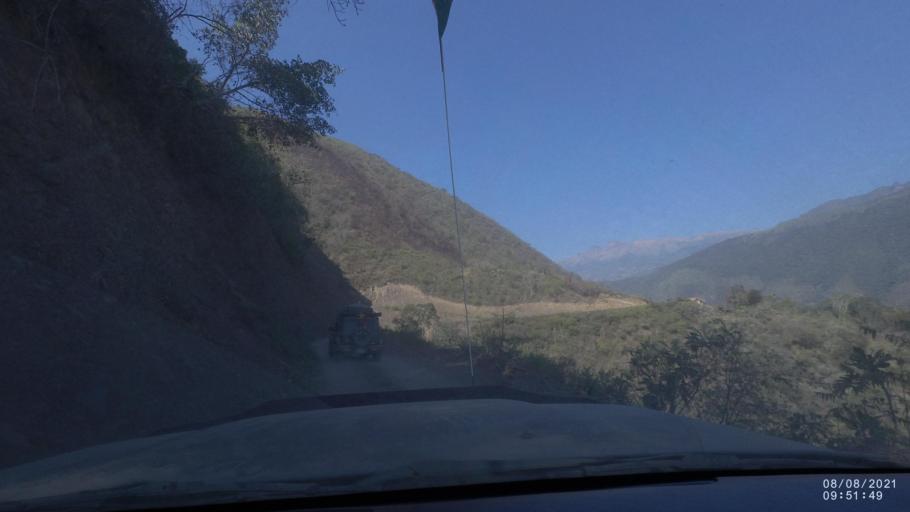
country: BO
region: La Paz
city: Quime
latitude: -16.6240
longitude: -66.7296
